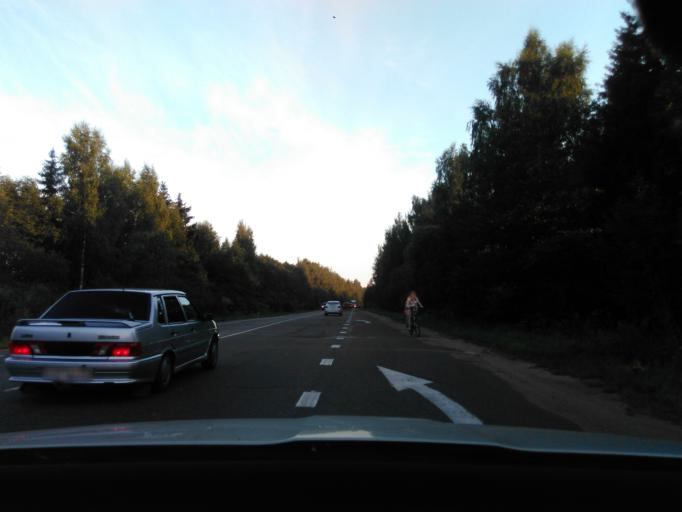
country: RU
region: Tverskaya
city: Konakovo
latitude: 56.6649
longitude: 36.7179
